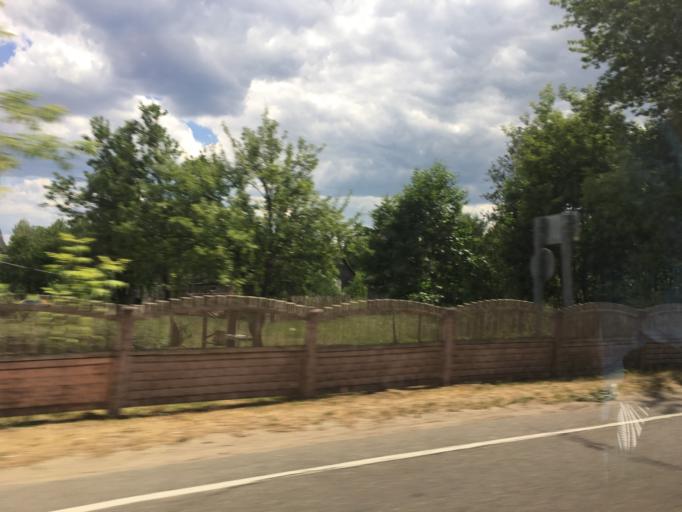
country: LT
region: Alytaus apskritis
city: Druskininkai
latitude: 53.8794
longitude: 24.1285
